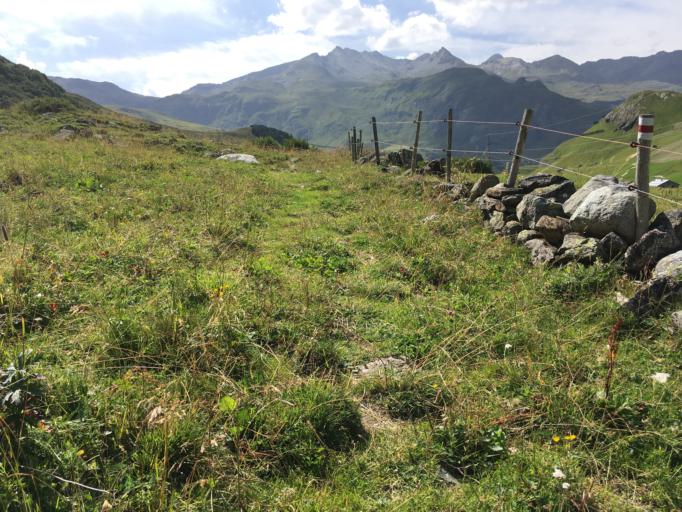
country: CH
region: Grisons
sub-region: Maloja District
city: Silvaplana
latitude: 46.4603
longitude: 9.6744
